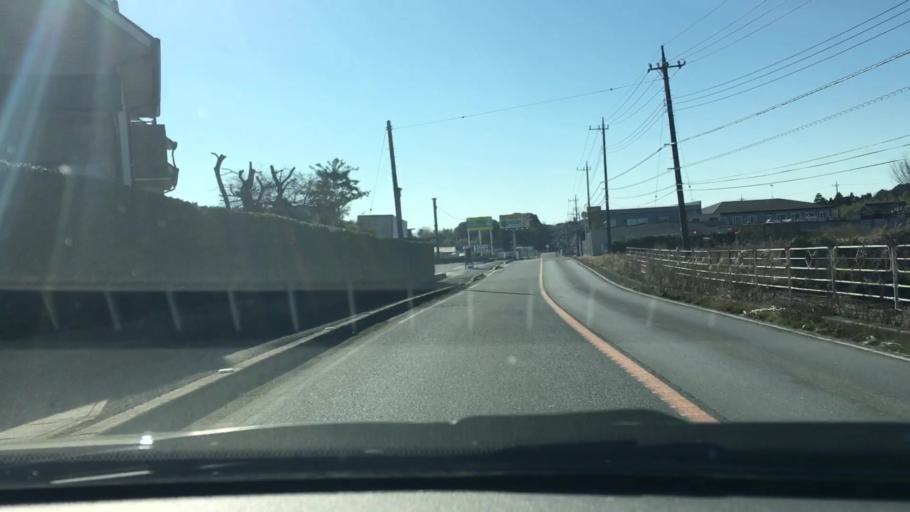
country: JP
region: Chiba
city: Shisui
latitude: 35.7039
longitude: 140.3141
